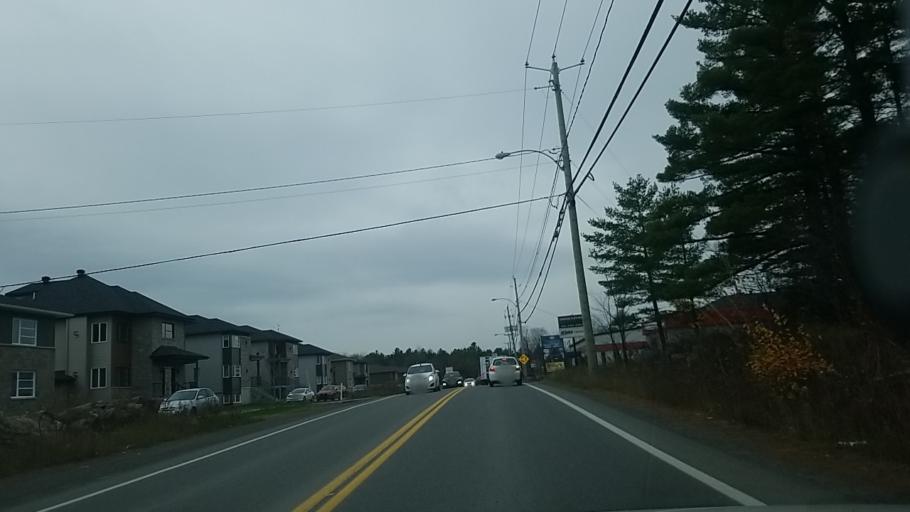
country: CA
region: Quebec
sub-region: Laurentides
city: Saint-Jerome
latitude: 45.7766
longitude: -74.0451
